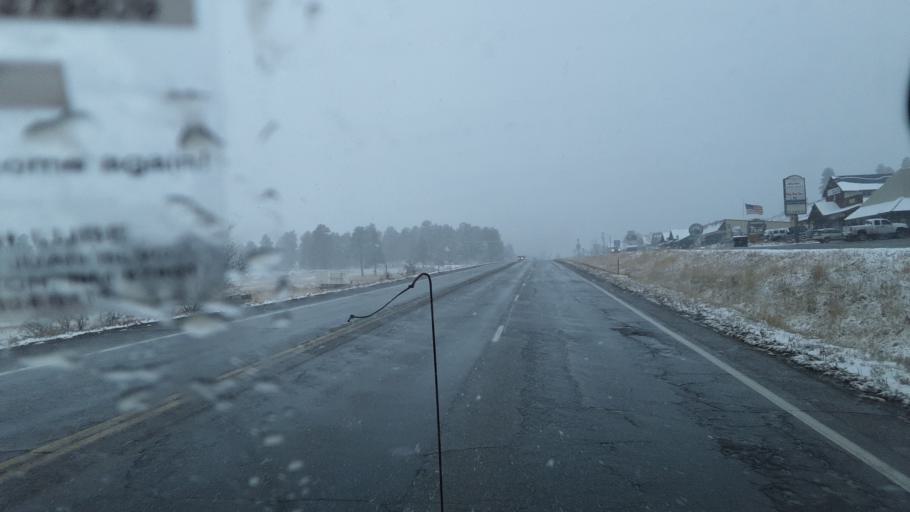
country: US
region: Colorado
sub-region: Archuleta County
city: Pagosa Springs
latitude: 37.2702
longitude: -107.0428
